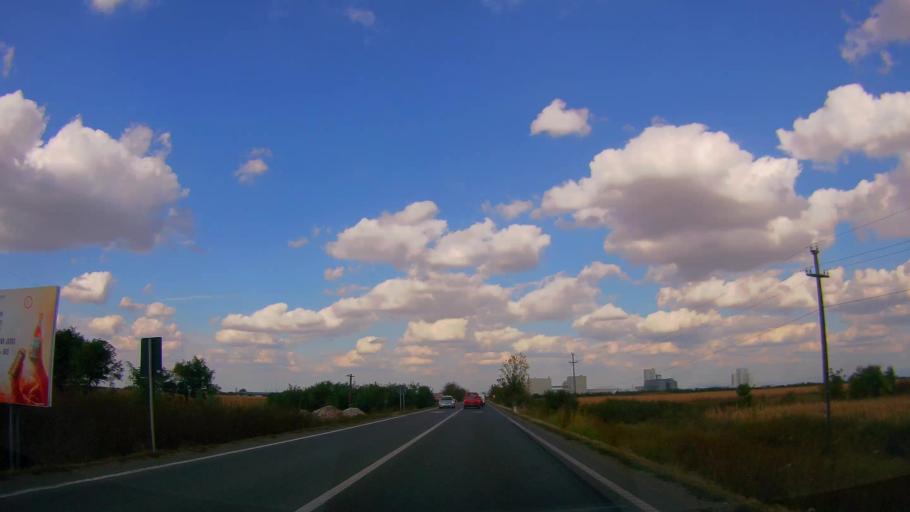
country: RO
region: Satu Mare
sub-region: Comuna Botiz
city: Botiz
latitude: 47.8164
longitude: 22.9306
